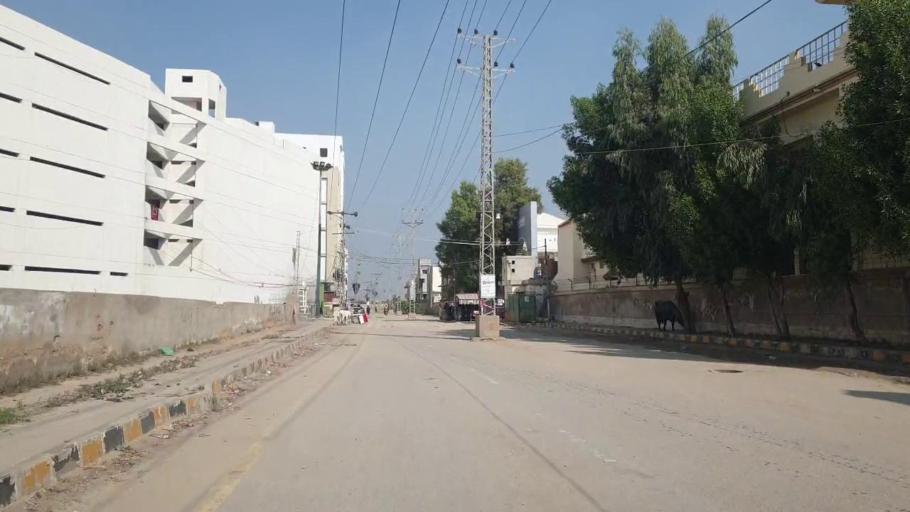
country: PK
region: Sindh
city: Hyderabad
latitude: 25.4219
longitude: 68.3547
